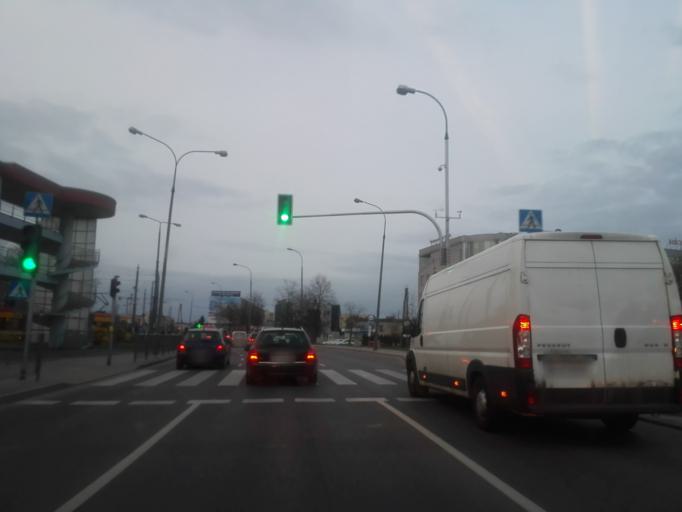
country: PL
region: Masovian Voivodeship
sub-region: Warszawa
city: Wlochy
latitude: 52.1750
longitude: 20.9441
